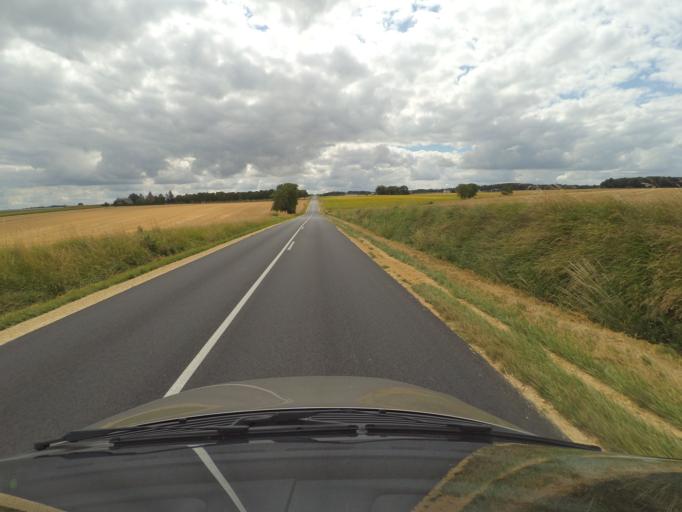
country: FR
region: Poitou-Charentes
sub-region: Departement de la Vienne
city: Saint-Gervais-les-Trois-Clochers
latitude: 46.9220
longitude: 0.4376
